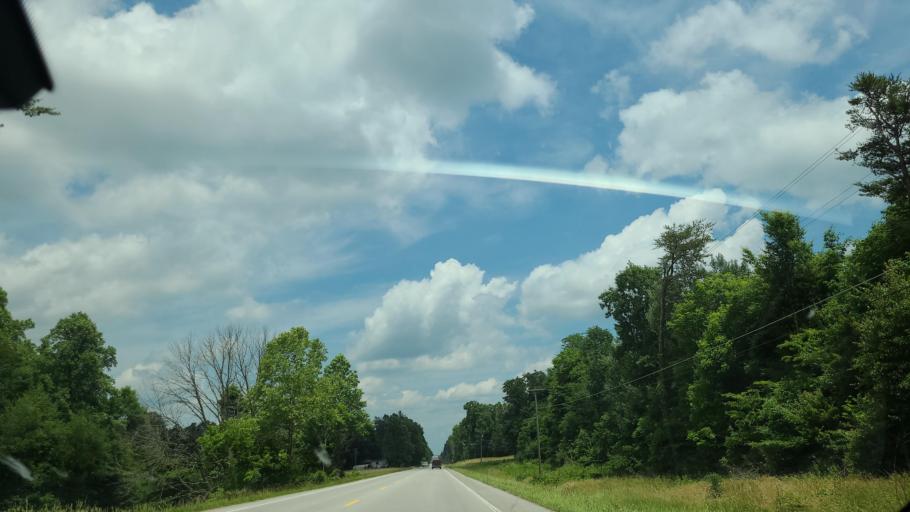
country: US
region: Tennessee
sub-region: Cumberland County
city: Lake Tansi
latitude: 35.7844
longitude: -85.0306
